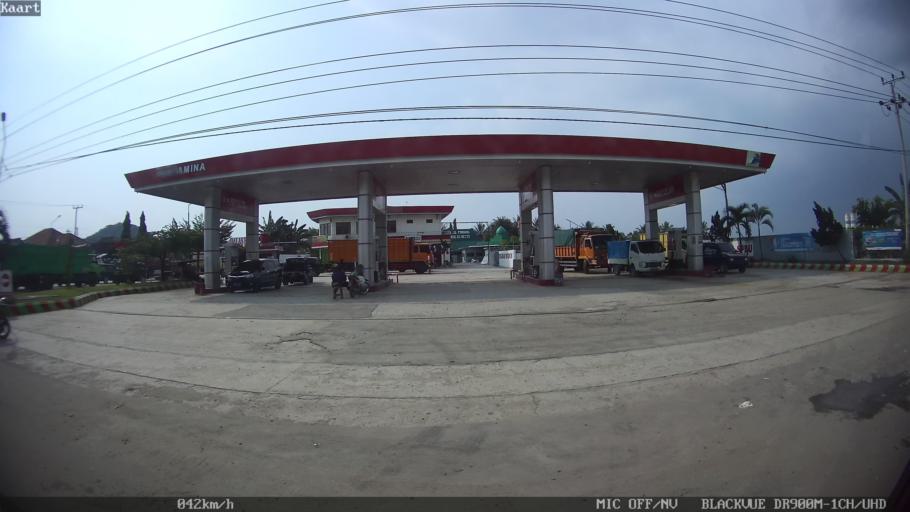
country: ID
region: Lampung
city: Gadingrejo
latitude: -5.3810
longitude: 105.0245
